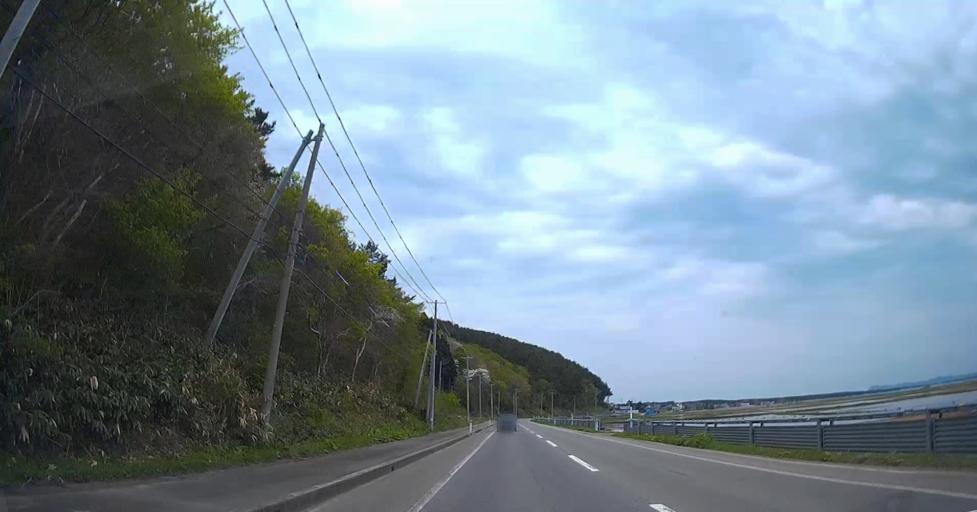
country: JP
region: Aomori
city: Shimokizukuri
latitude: 40.9956
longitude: 140.3513
